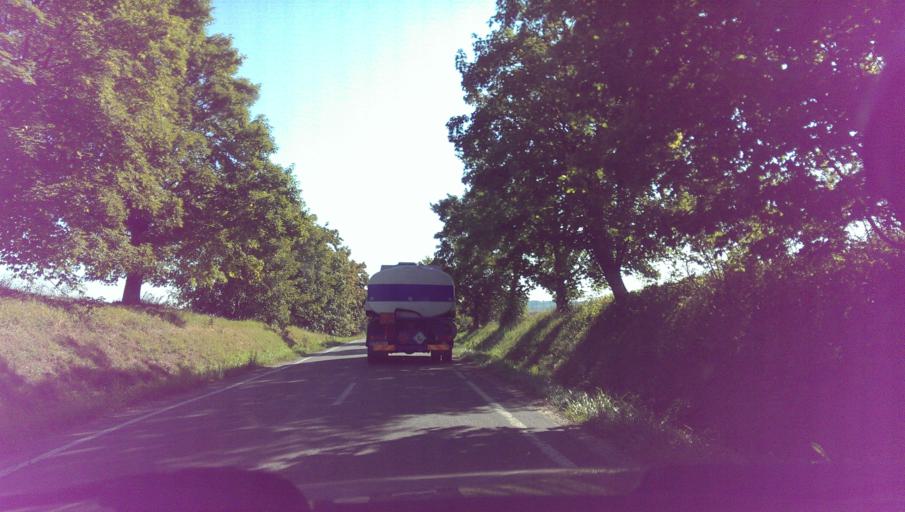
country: CZ
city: Brusperk
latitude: 49.6891
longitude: 18.2136
